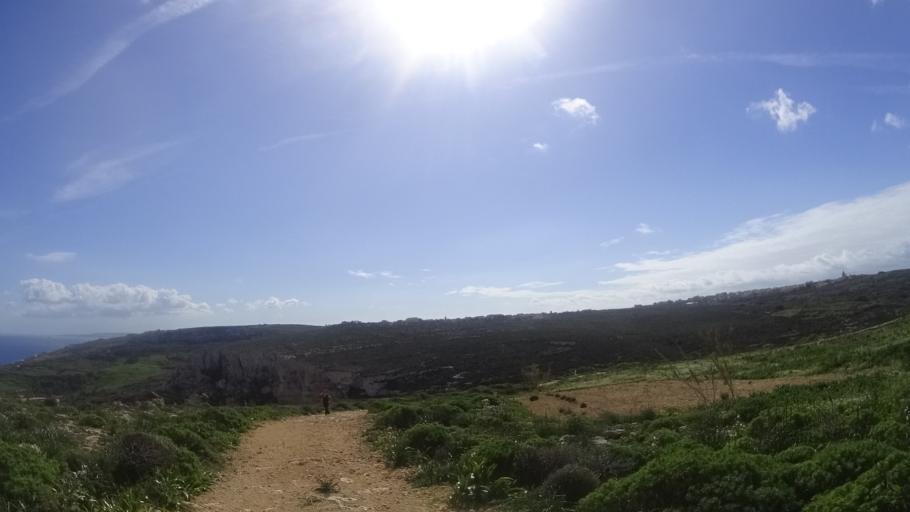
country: MT
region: Il-Qala
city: Qala
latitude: 36.0543
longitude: 14.3083
